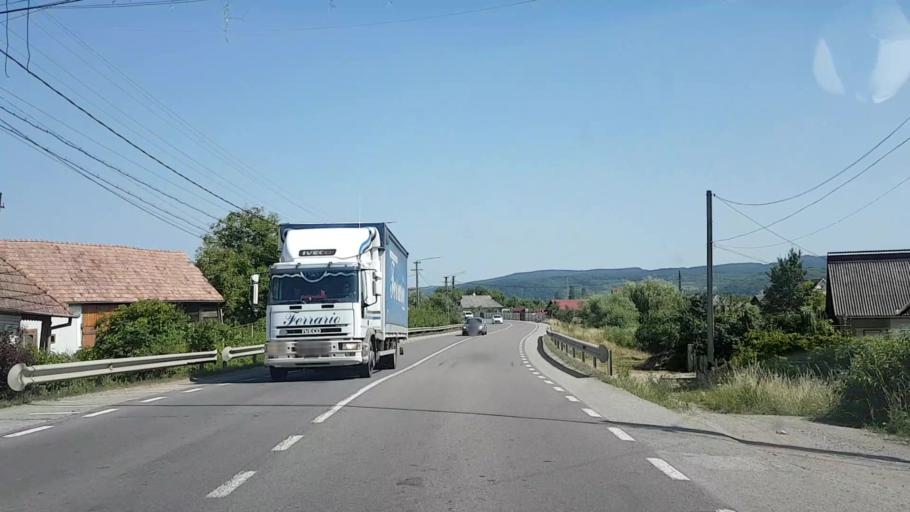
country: RO
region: Bistrita-Nasaud
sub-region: Comuna Uriu
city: Cristestii Ciceului
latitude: 47.1924
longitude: 24.0965
